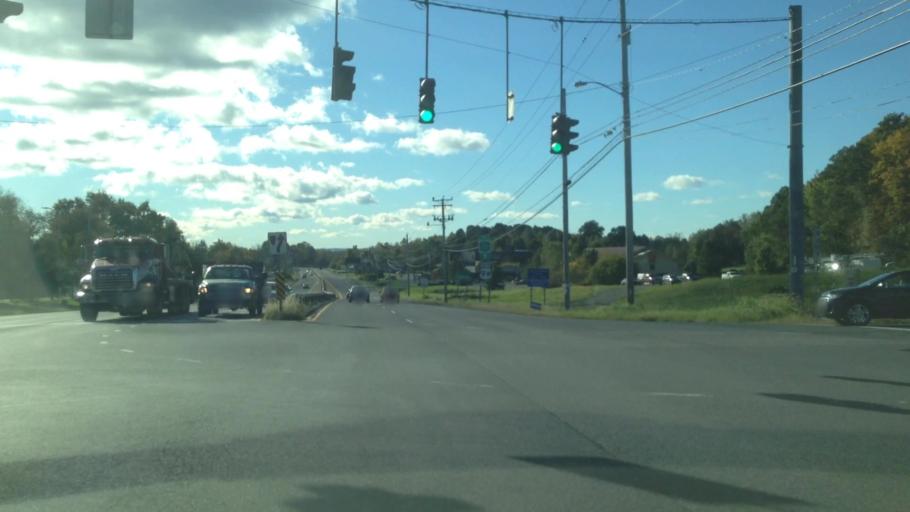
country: US
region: New York
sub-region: Ulster County
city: Highland
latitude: 41.7422
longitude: -73.9644
